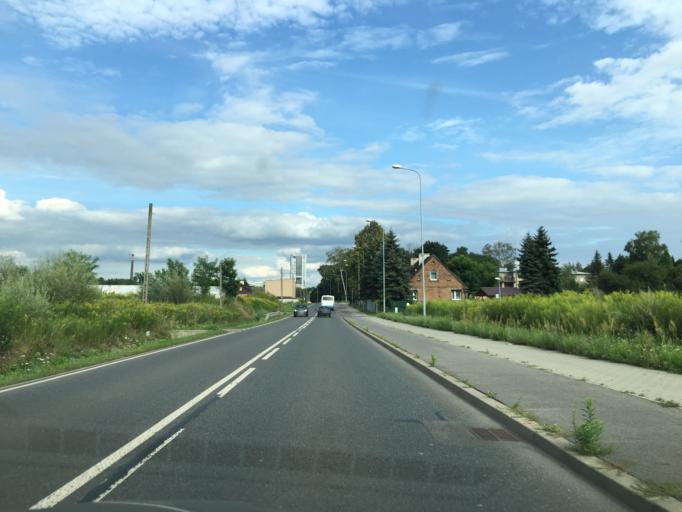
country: PL
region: Silesian Voivodeship
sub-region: Ruda Slaska
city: Ruda Slaska
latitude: 50.2650
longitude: 18.8158
